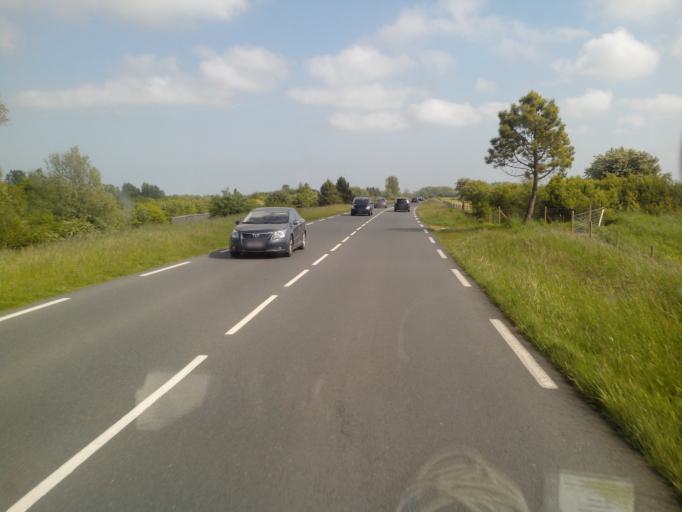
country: FR
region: Picardie
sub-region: Departement de la Somme
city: Saint-Valery-sur-Somme
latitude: 50.2049
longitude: 1.6832
